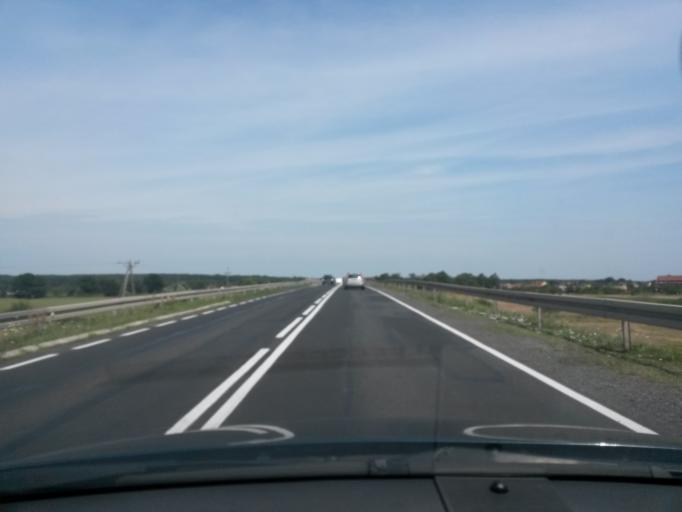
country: PL
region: Lower Silesian Voivodeship
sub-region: Powiat legnicki
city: Prochowice
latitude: 51.2798
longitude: 16.3479
